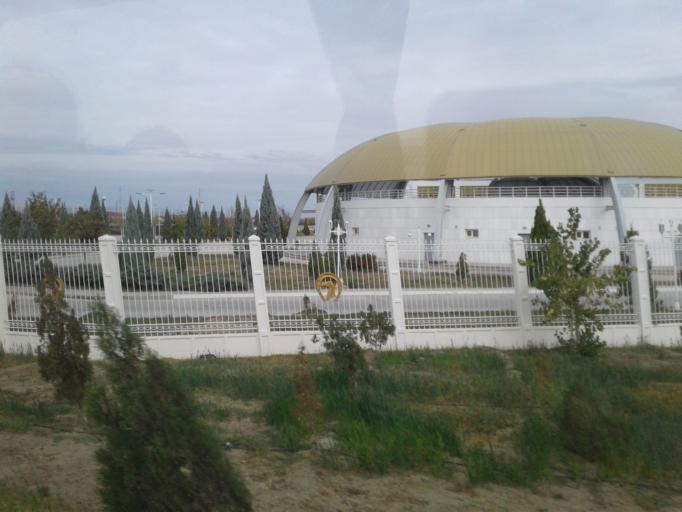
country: TM
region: Lebap
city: Turkmenabat
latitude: 38.9899
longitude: 63.5595
